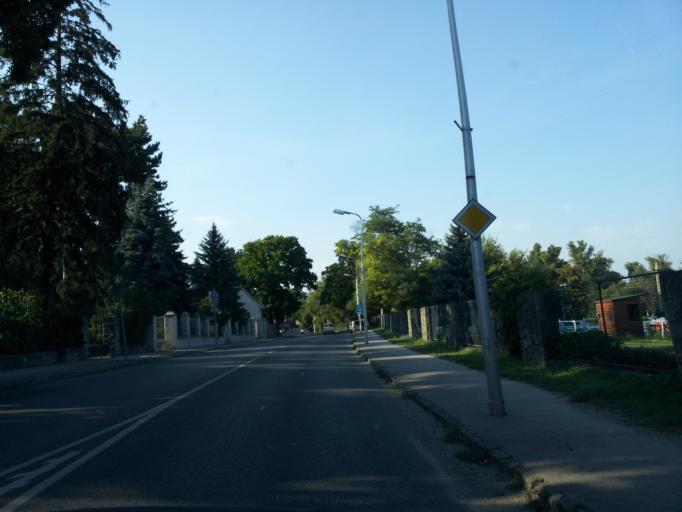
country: HU
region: Pest
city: Leanyfalu
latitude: 47.7208
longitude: 19.0890
